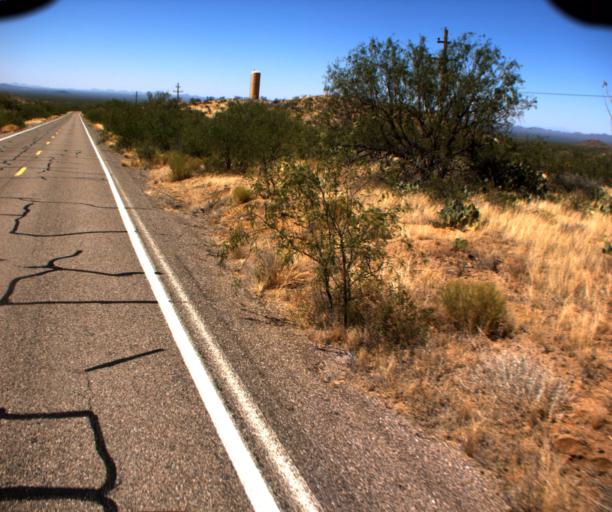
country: US
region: Arizona
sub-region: Pima County
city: Three Points
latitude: 32.0026
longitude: -111.5721
